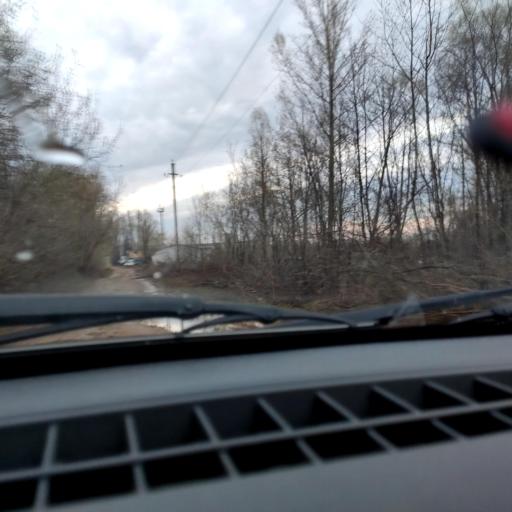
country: RU
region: Bashkortostan
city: Ufa
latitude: 54.6764
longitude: 55.9507
